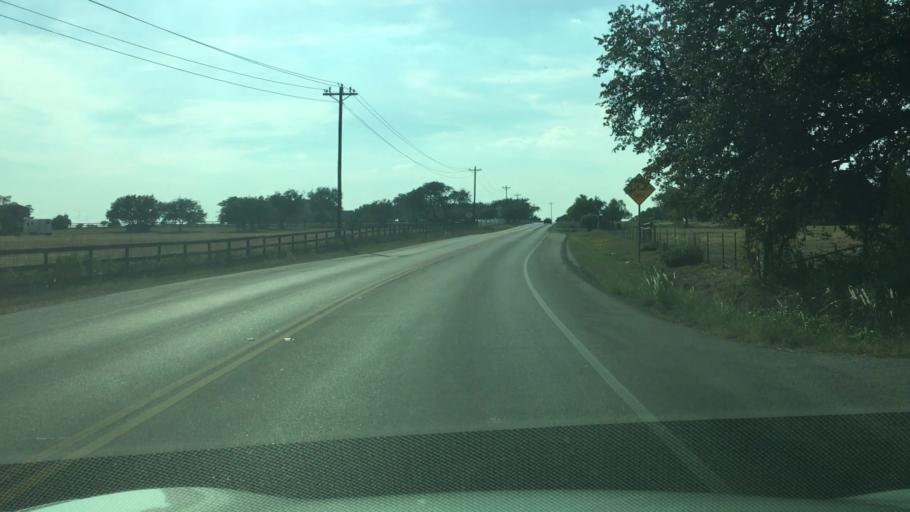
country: US
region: Texas
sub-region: Hays County
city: Dripping Springs
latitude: 30.1476
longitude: -97.9877
